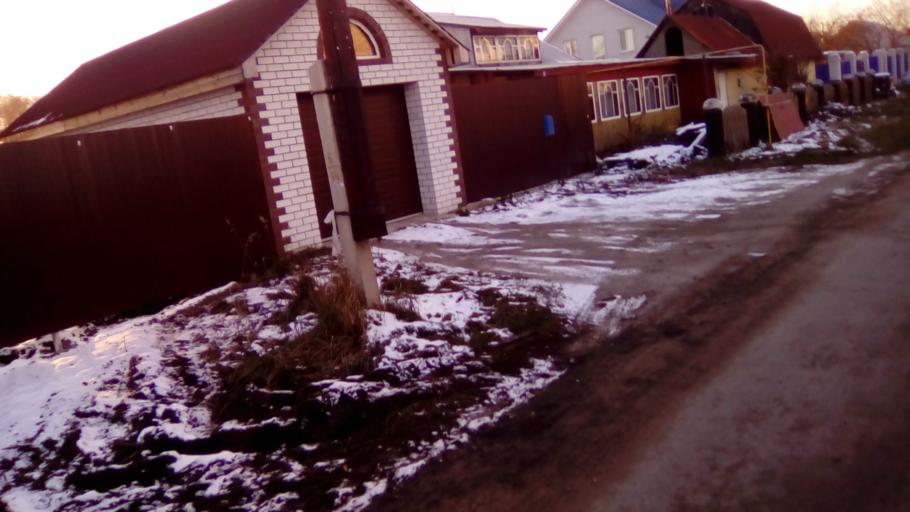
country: RU
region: Tjumen
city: Moskovskiy
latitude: 57.2206
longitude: 65.3655
